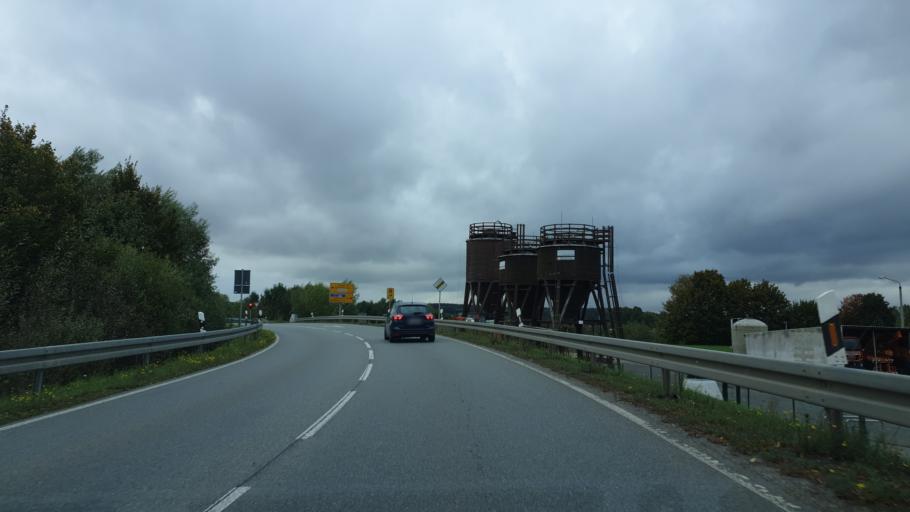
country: DE
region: Saxony
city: Glauchau
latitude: 50.8338
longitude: 12.5527
